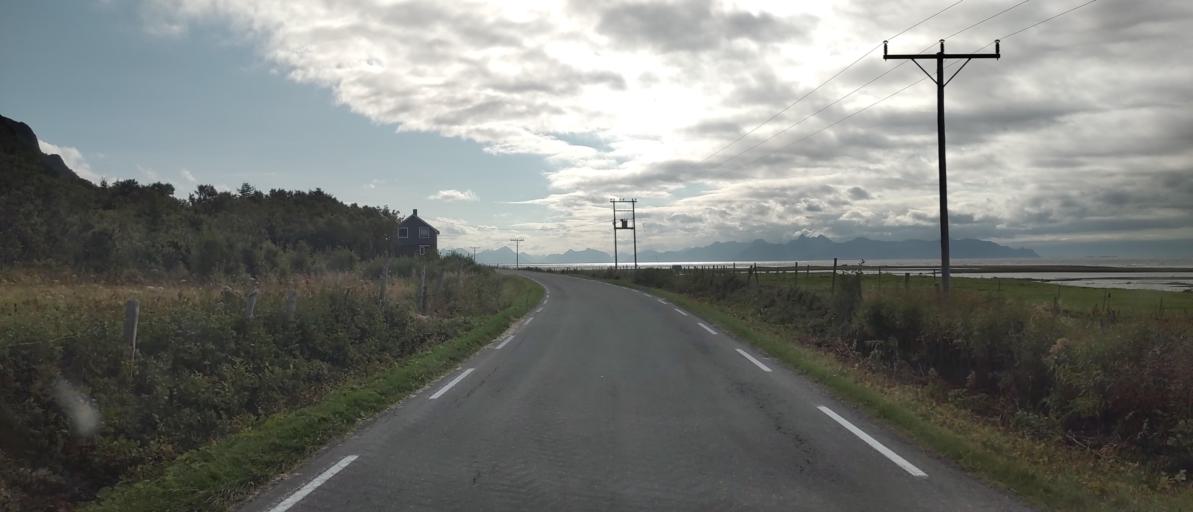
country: NO
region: Nordland
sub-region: Sortland
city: Sortland
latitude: 69.0699
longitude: 15.5448
